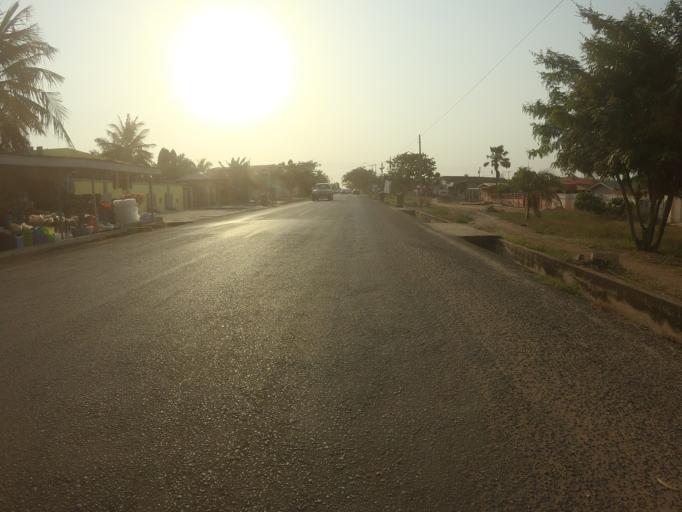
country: GH
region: Greater Accra
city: Nungua
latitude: 5.6165
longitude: -0.0502
